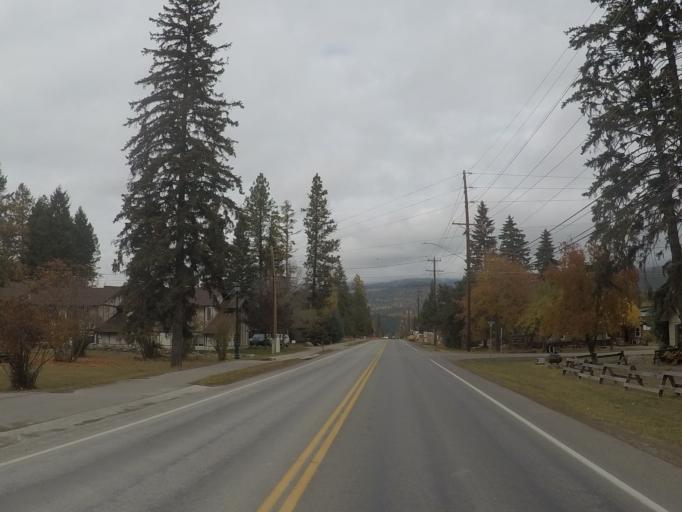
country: US
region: Montana
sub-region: Flathead County
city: Whitefish
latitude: 48.4203
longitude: -114.3411
